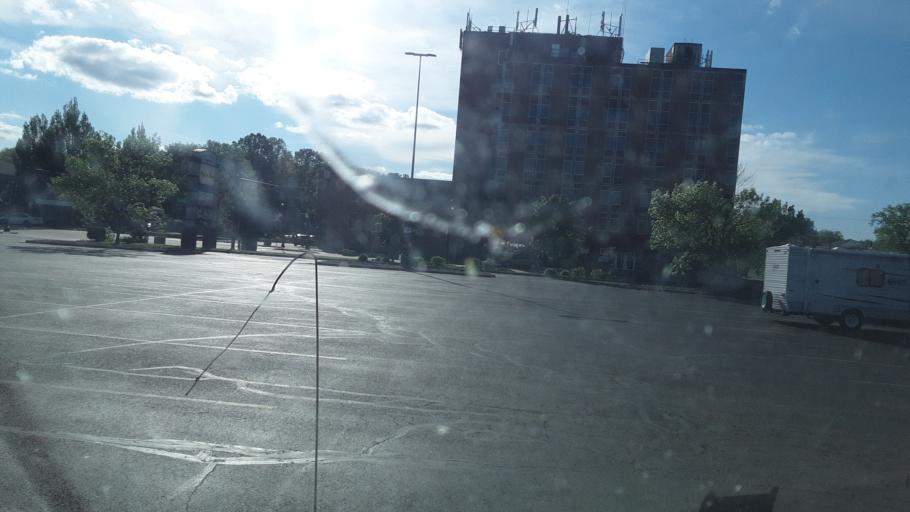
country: US
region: Wisconsin
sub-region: Wood County
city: Marshfield
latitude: 44.6613
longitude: -90.1764
